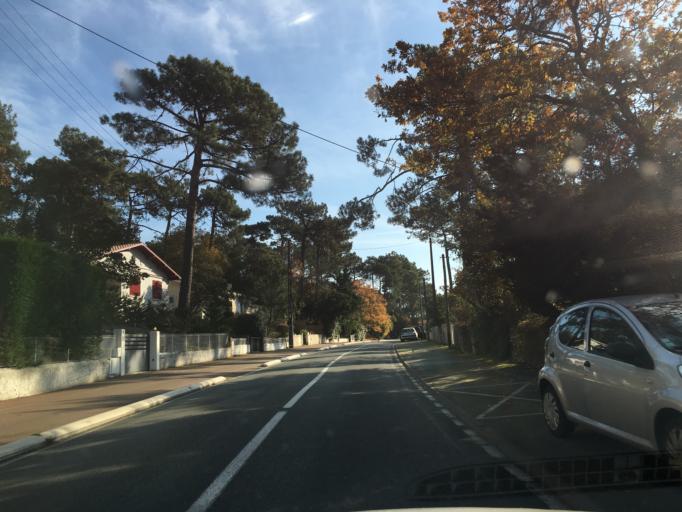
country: FR
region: Aquitaine
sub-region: Departement de la Gironde
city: Arcachon
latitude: 44.6436
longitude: -1.1749
